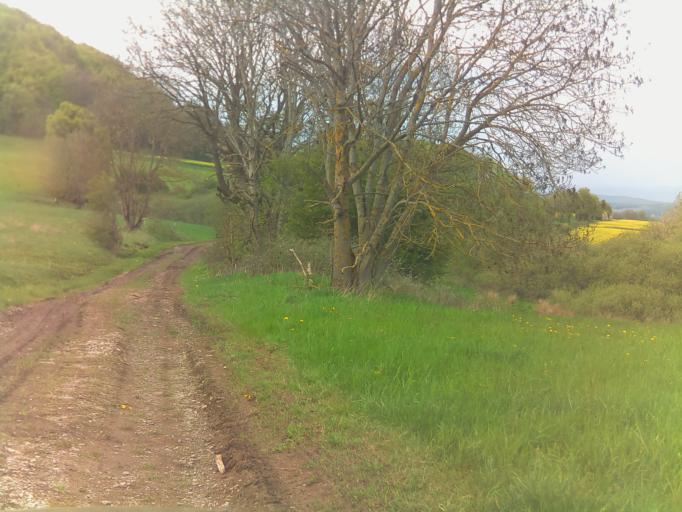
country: DE
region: Thuringia
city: Oepfershausen
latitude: 50.6294
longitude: 10.2370
